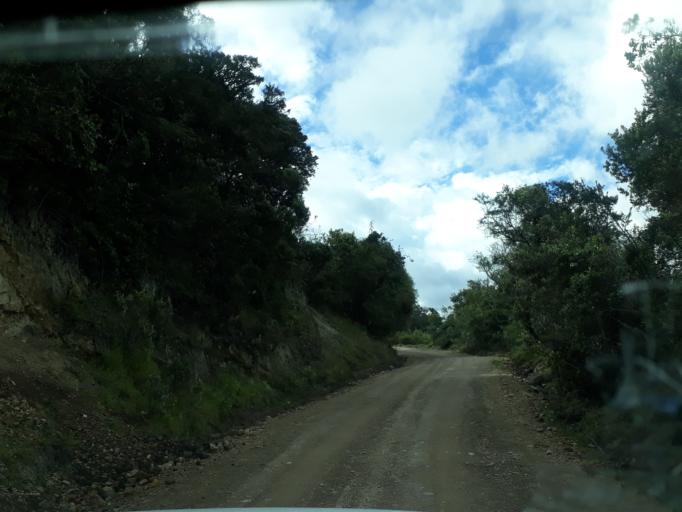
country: CO
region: Cundinamarca
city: La Mesa
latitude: 5.2512
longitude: -73.8948
